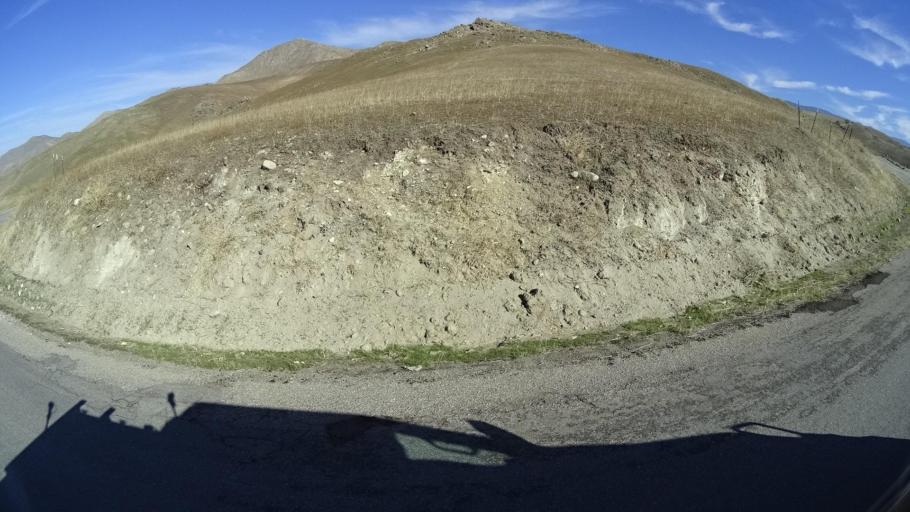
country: US
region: California
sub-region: Kern County
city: Arvin
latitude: 35.4115
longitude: -118.7513
